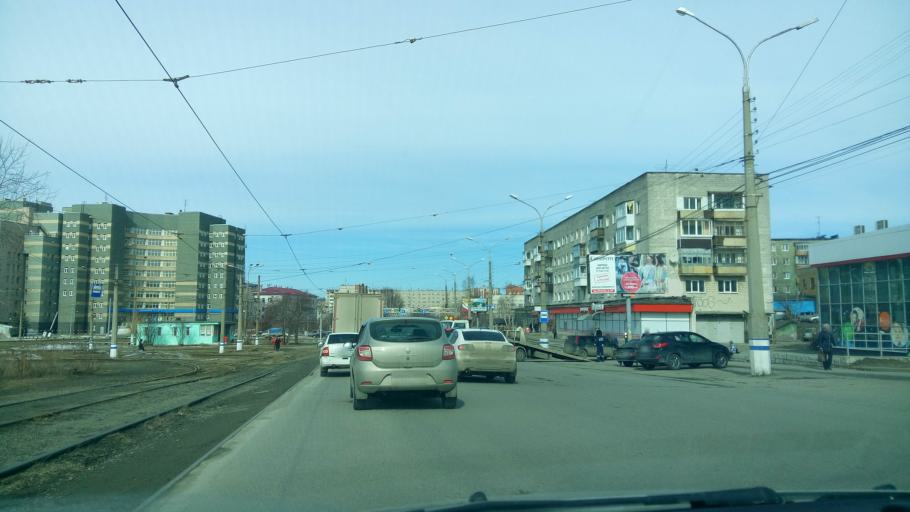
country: RU
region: Sverdlovsk
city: Nizhniy Tagil
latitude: 57.9074
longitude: 59.9485
